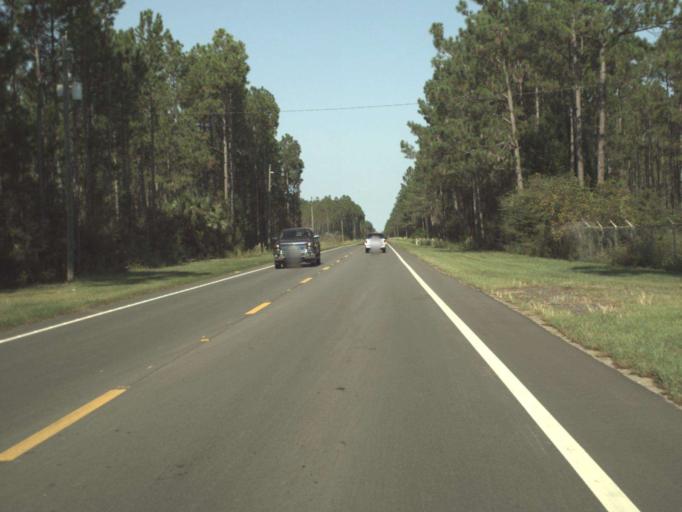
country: US
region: Florida
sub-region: Gulf County
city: Port Saint Joe
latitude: 29.8493
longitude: -85.2586
